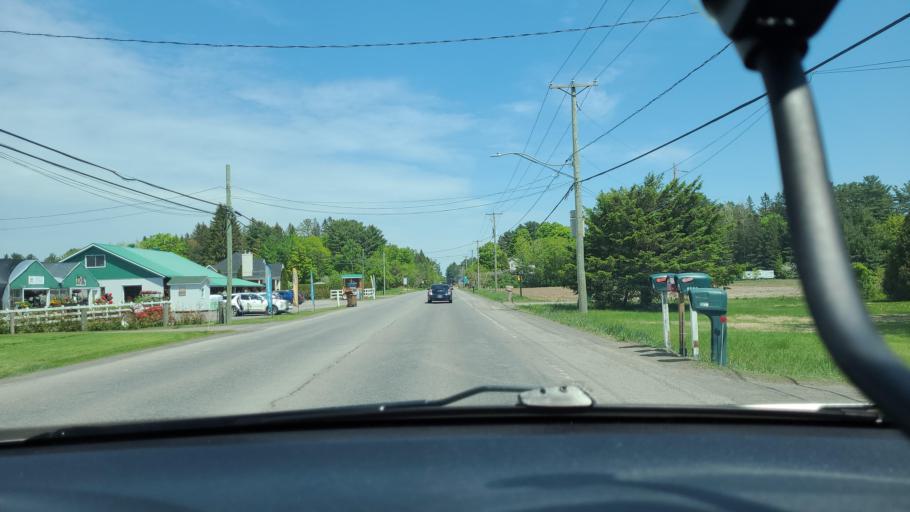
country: CA
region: Quebec
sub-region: Laurentides
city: Lachute
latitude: 45.6632
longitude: -74.3021
